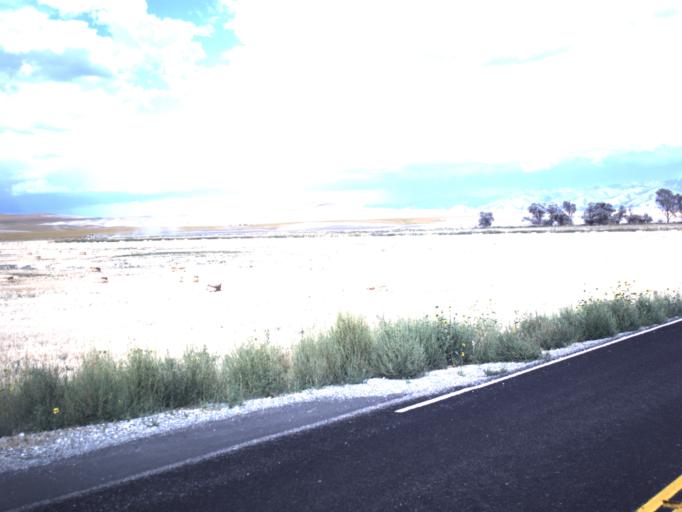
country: US
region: Utah
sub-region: Cache County
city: Benson
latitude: 41.9197
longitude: -112.0314
